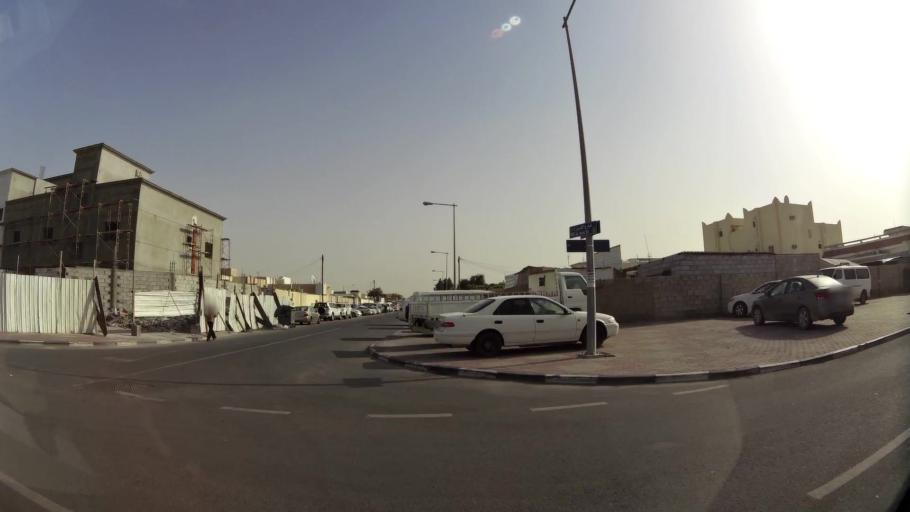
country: QA
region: Baladiyat ar Rayyan
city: Ar Rayyan
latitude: 25.2358
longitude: 51.4359
